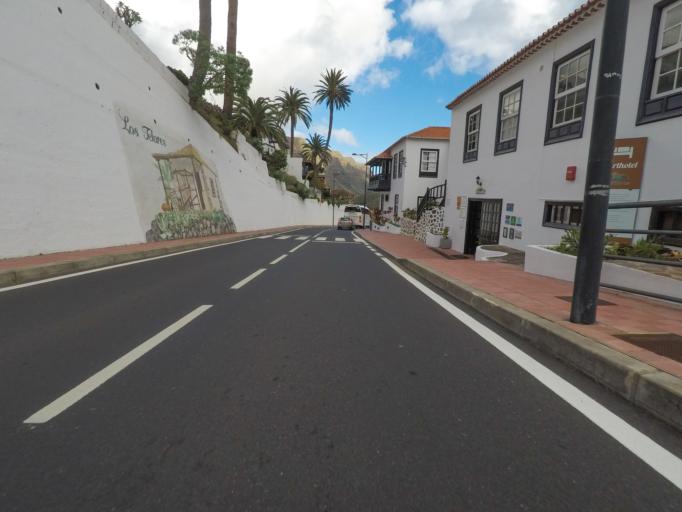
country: ES
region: Canary Islands
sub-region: Provincia de Santa Cruz de Tenerife
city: Hermigua
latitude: 28.1514
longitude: -17.1981
